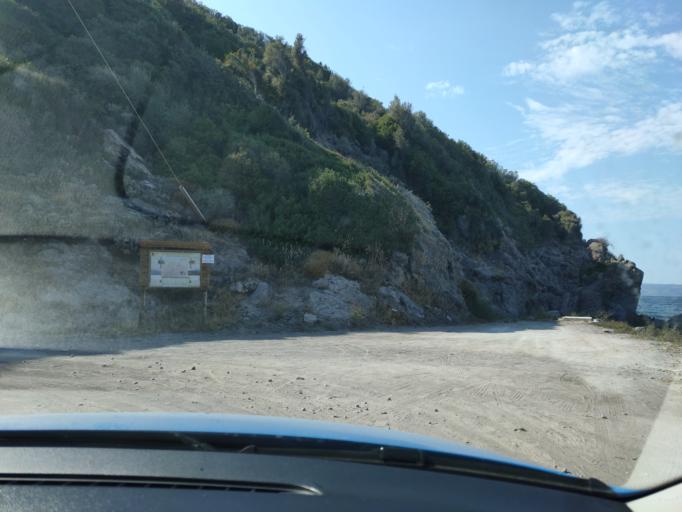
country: GR
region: North Aegean
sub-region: Nomos Lesvou
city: Mantamados
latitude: 39.3749
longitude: 26.3093
